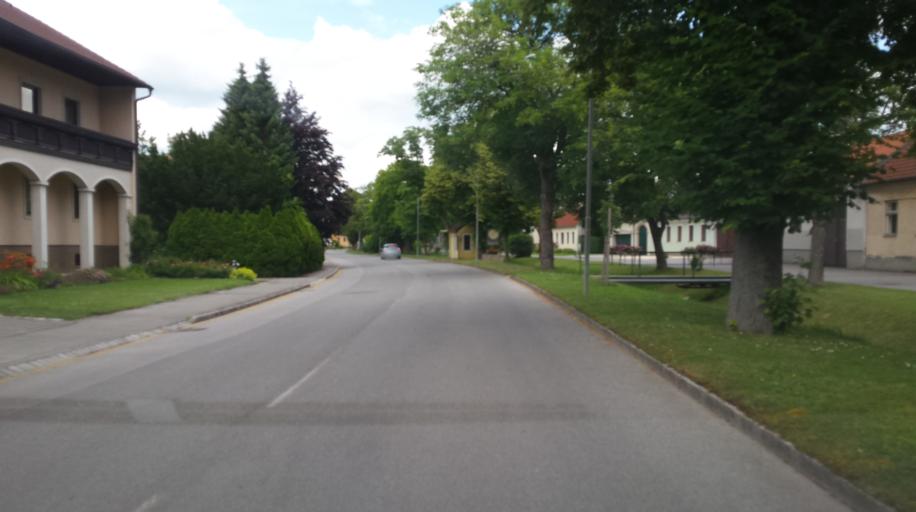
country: AT
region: Lower Austria
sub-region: Politischer Bezirk Mistelbach
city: Hochleithen
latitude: 48.4426
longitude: 16.5185
